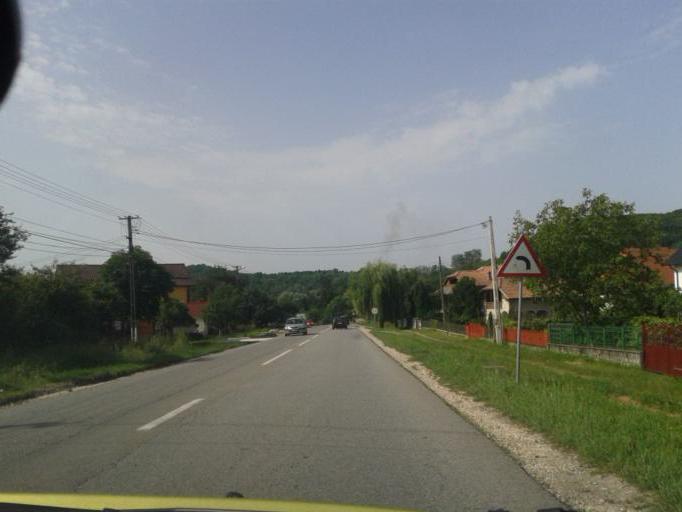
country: RO
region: Valcea
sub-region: Comuna Pietrari
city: Pietrarii de Sus
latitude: 45.1144
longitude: 24.1154
